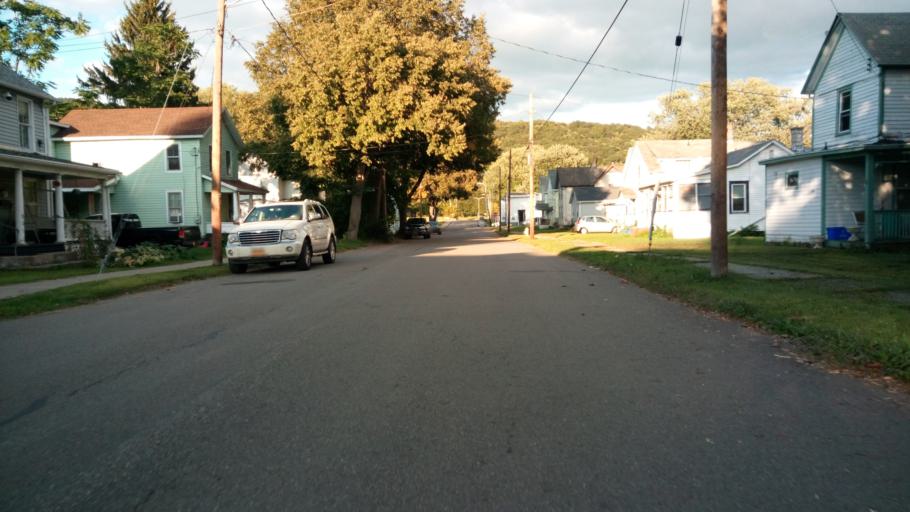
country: US
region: New York
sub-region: Chemung County
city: Elmira
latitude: 42.1039
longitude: -76.8010
